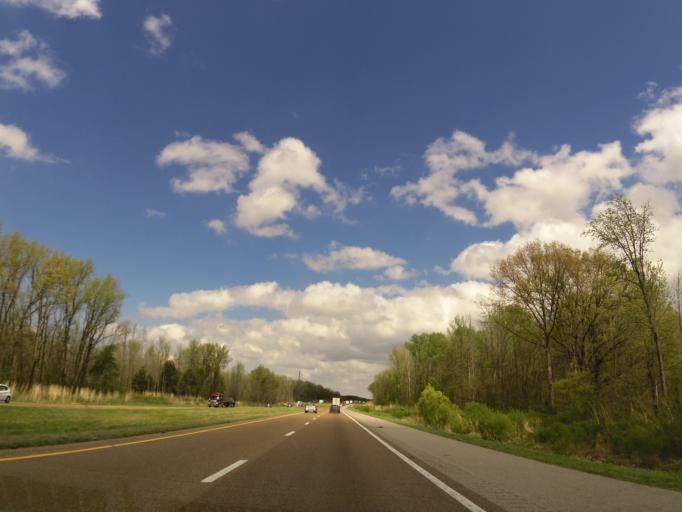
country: US
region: Tennessee
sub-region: Tipton County
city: Mason
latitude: 35.3280
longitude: -89.5602
